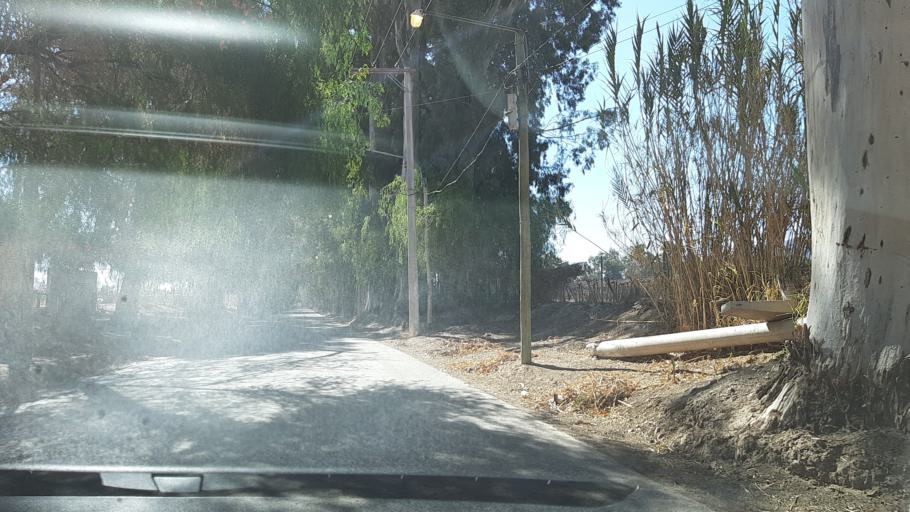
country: AR
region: San Juan
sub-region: Departamento de Zonda
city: Zonda
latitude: -31.5688
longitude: -68.7357
